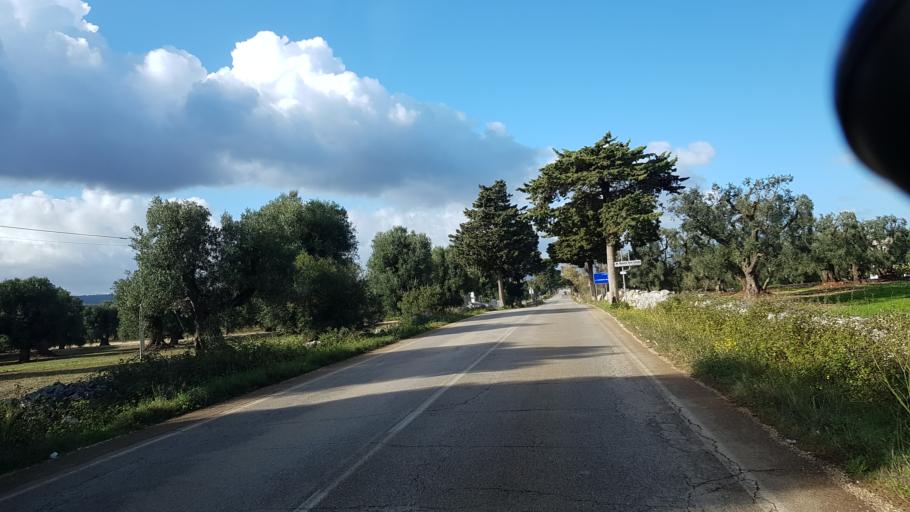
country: IT
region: Apulia
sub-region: Provincia di Brindisi
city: Montalbano
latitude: 40.7965
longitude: 17.4491
